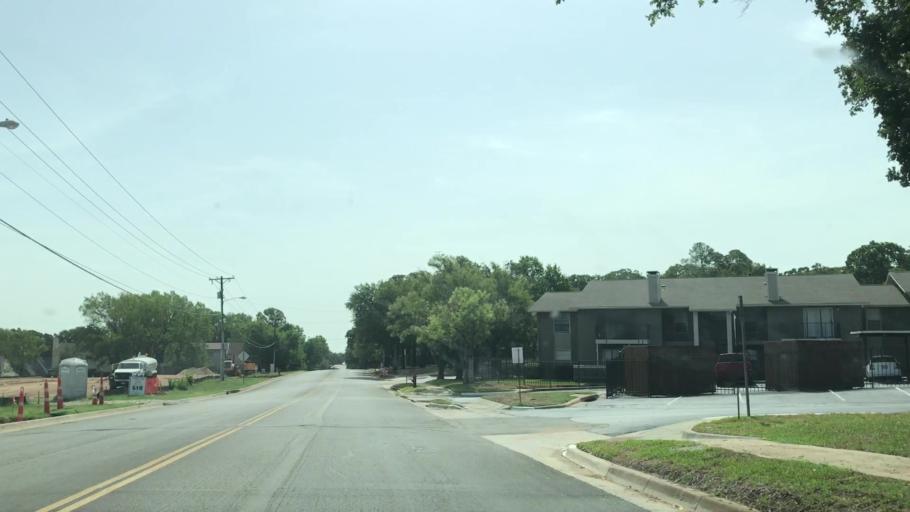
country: US
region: Texas
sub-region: Tarrant County
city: Euless
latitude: 32.8590
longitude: -97.0799
